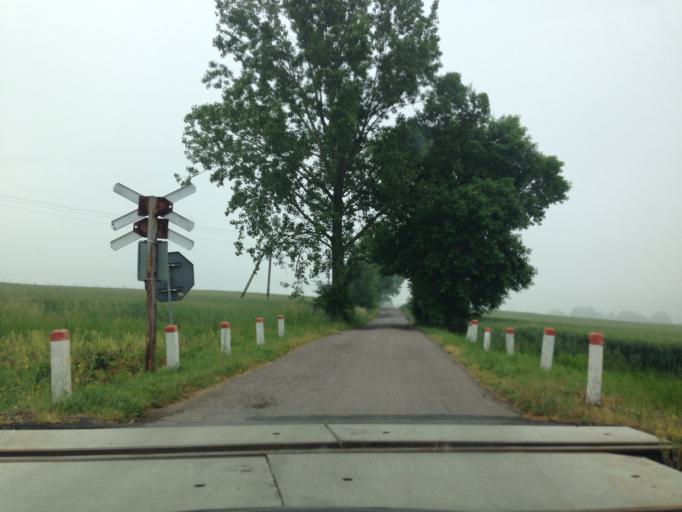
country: PL
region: Kujawsko-Pomorskie
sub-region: Powiat brodnicki
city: Jablonowo Pomorskie
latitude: 53.4061
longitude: 19.2209
